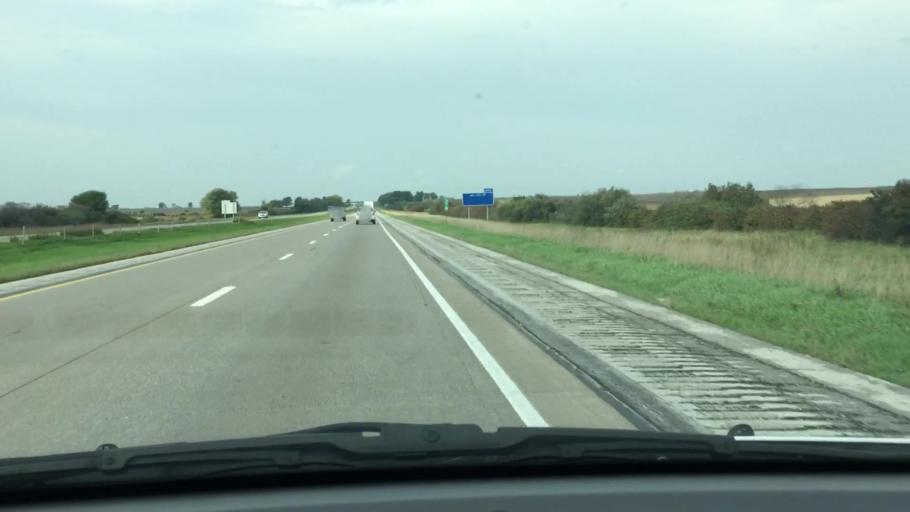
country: US
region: Iowa
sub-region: Cedar County
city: Durant
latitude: 41.6331
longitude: -90.8814
